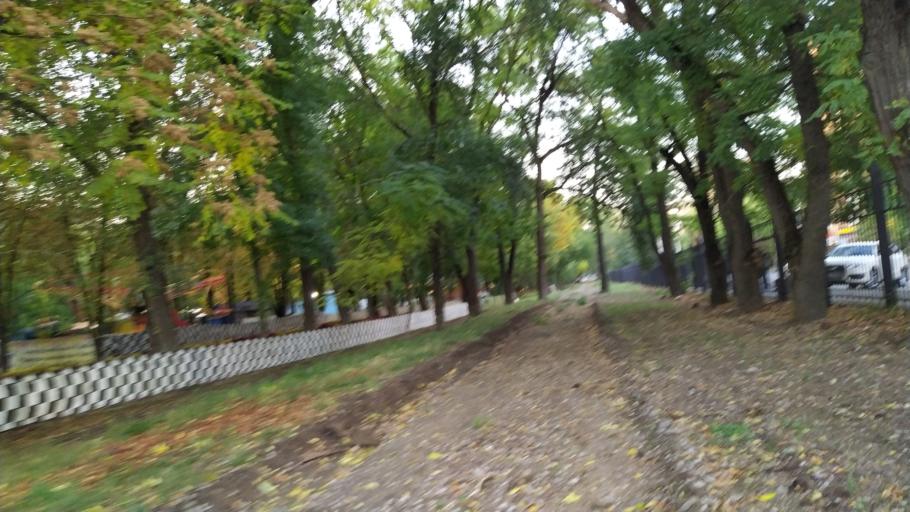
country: RU
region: Rostov
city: Imeni Chkalova
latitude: 47.2446
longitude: 39.7650
